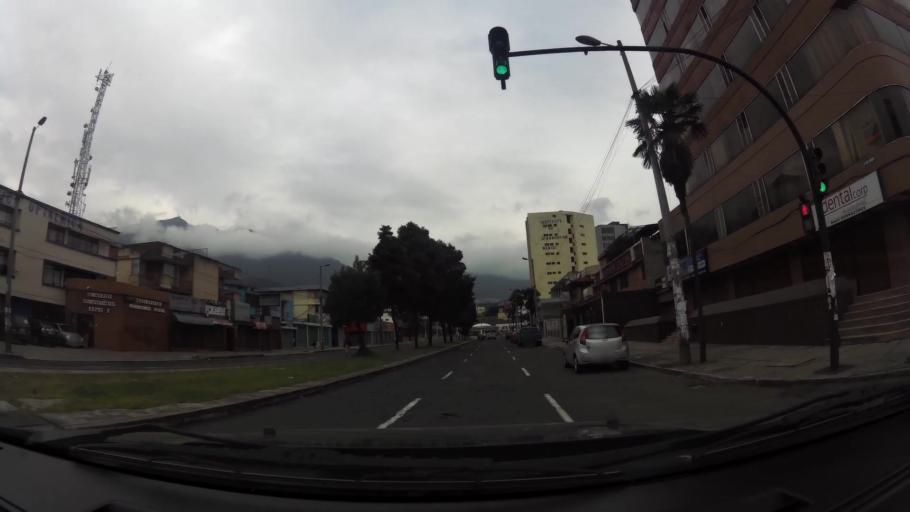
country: EC
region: Pichincha
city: Quito
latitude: -0.2036
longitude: -78.5007
